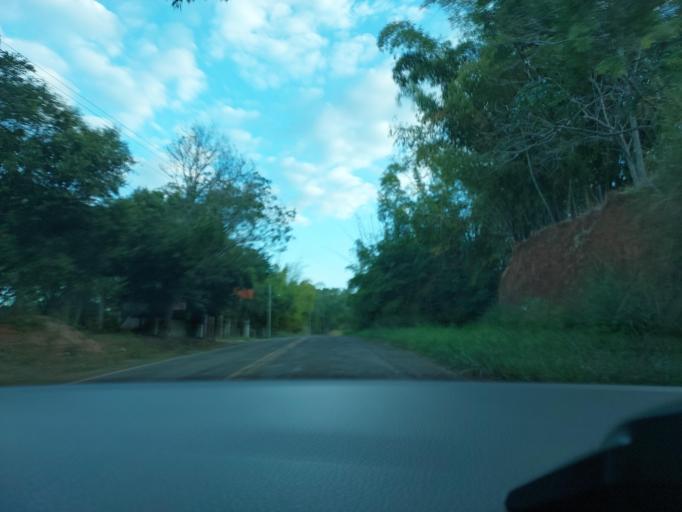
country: BR
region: Rio de Janeiro
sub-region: Natividade
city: Natividade
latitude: -21.1882
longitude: -42.1053
